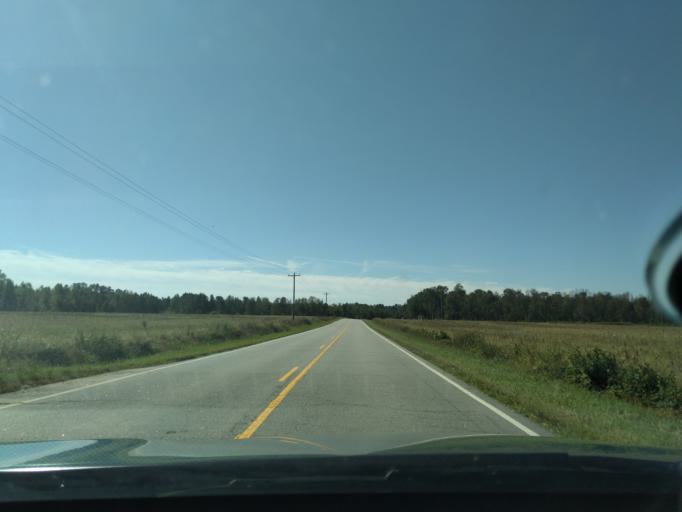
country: US
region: North Carolina
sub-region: Washington County
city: Plymouth
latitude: 35.7379
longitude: -76.7417
